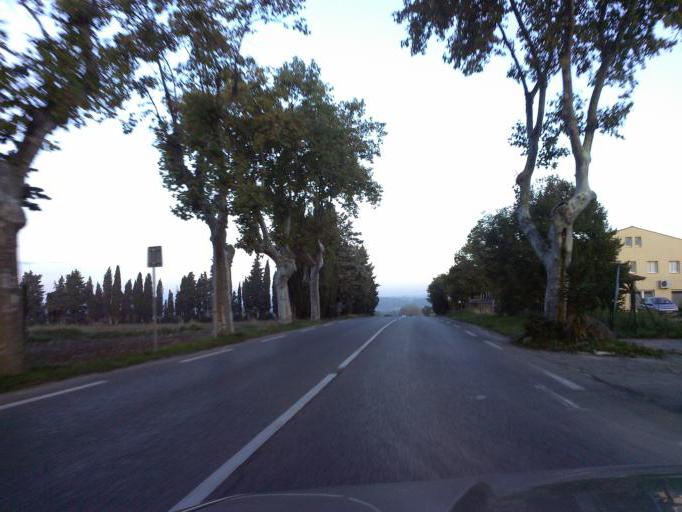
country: FR
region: Provence-Alpes-Cote d'Azur
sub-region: Departement des Bouches-du-Rhone
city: Saint-Cannat
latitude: 43.6252
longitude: 5.2932
